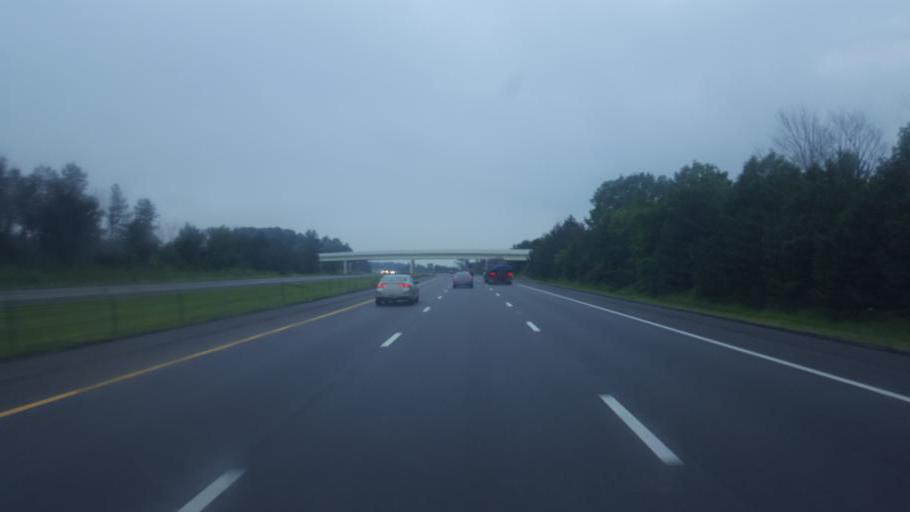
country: US
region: Ohio
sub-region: Morrow County
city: Cardington
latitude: 40.4391
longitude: -82.8066
